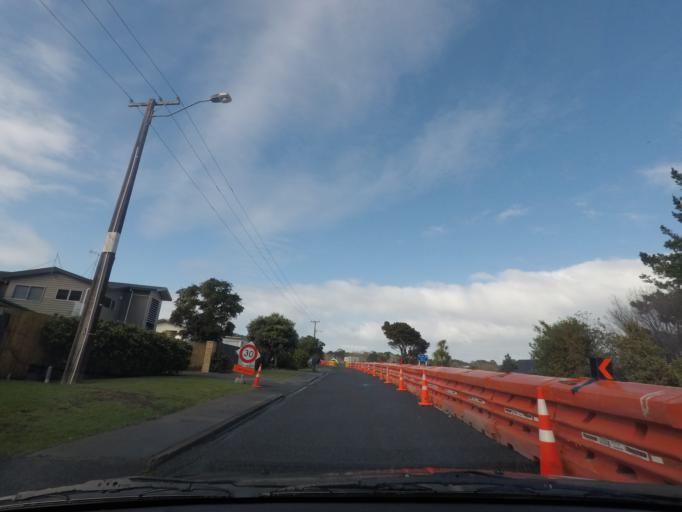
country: NZ
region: Auckland
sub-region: Auckland
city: Warkworth
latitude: -36.4334
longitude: 174.7386
